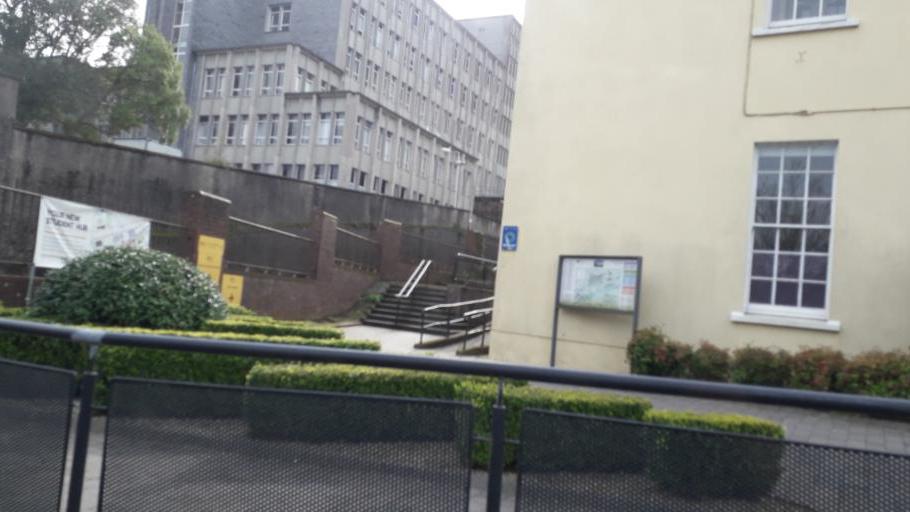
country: IE
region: Munster
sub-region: County Cork
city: Cork
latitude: 51.8933
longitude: -8.4952
